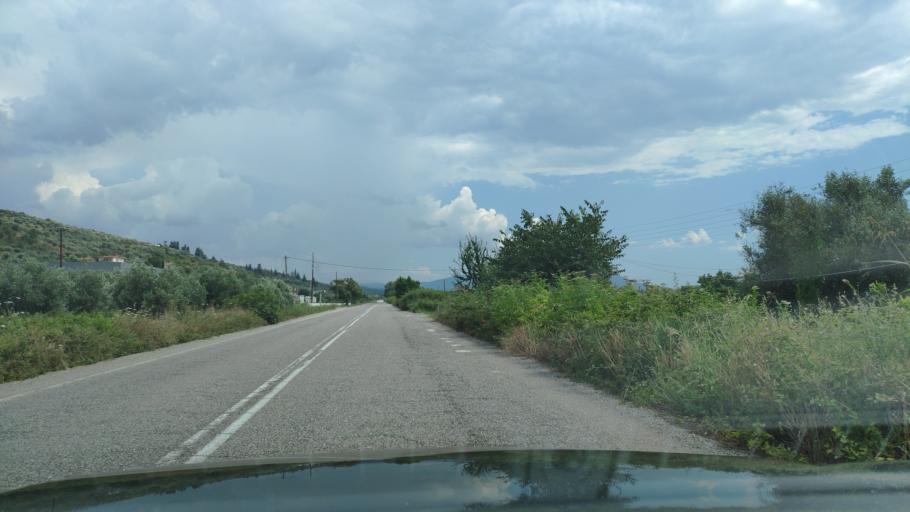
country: GR
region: West Greece
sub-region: Nomos Aitolias kai Akarnanias
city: Krikellos
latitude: 38.9645
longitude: 21.1697
